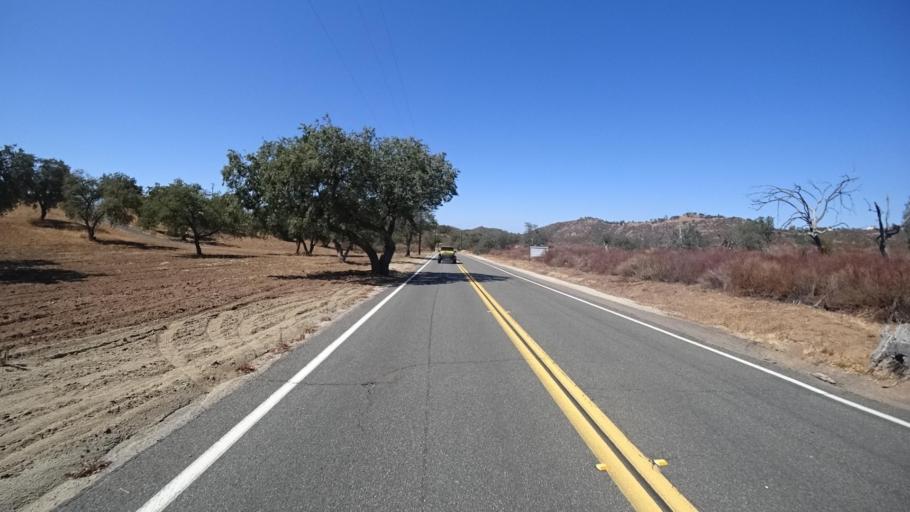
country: US
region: California
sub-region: San Diego County
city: San Diego Country Estates
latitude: 33.0580
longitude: -116.7687
